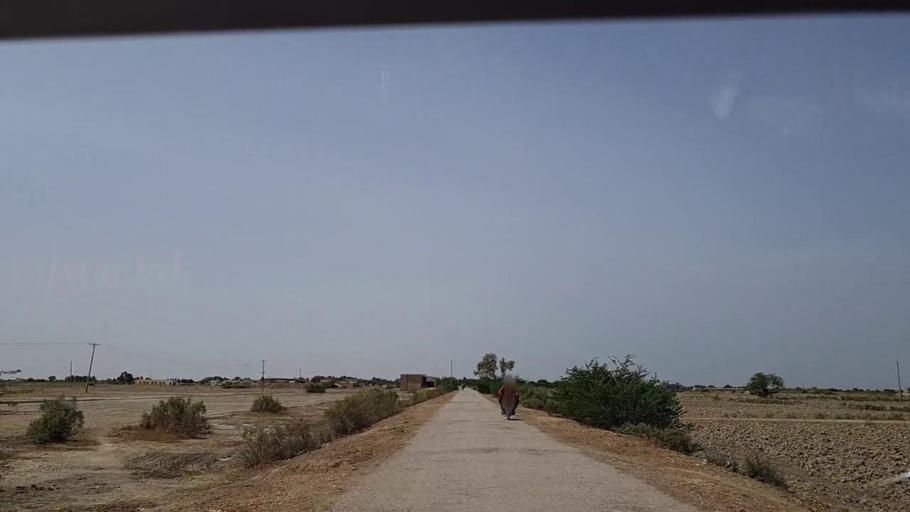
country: PK
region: Sindh
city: Johi
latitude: 26.7748
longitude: 67.6202
